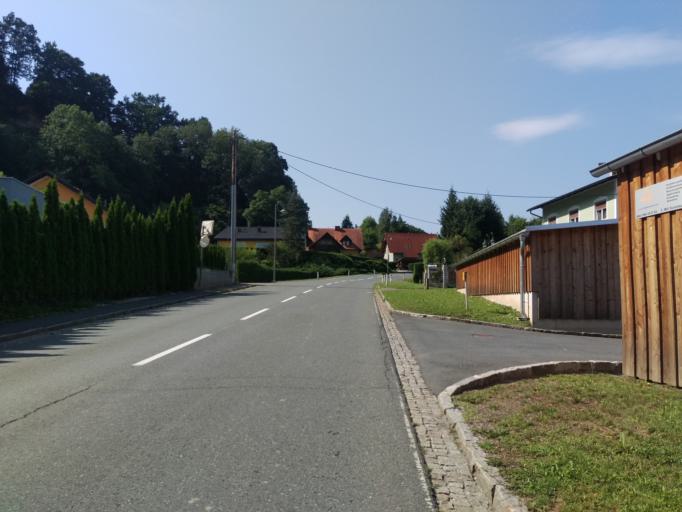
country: AT
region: Styria
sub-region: Politischer Bezirk Graz-Umgebung
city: Mellach
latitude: 46.9414
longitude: 15.5111
